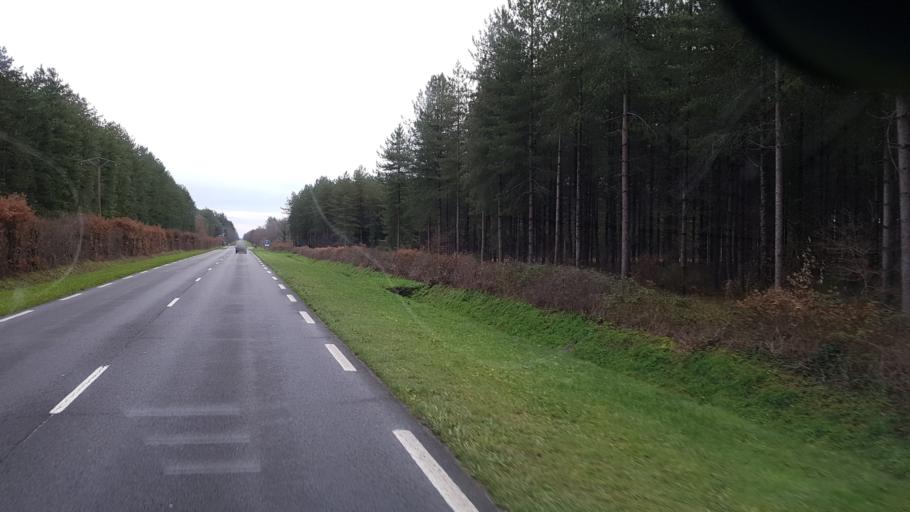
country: FR
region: Centre
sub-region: Departement du Loir-et-Cher
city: Lamotte-Beuvron
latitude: 47.6347
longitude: 2.0016
